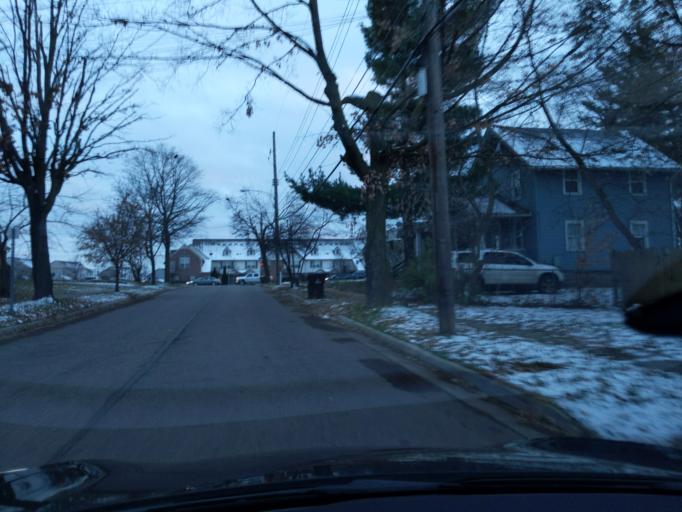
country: US
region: Michigan
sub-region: Ingham County
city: Lansing
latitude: 42.7417
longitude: -84.5336
